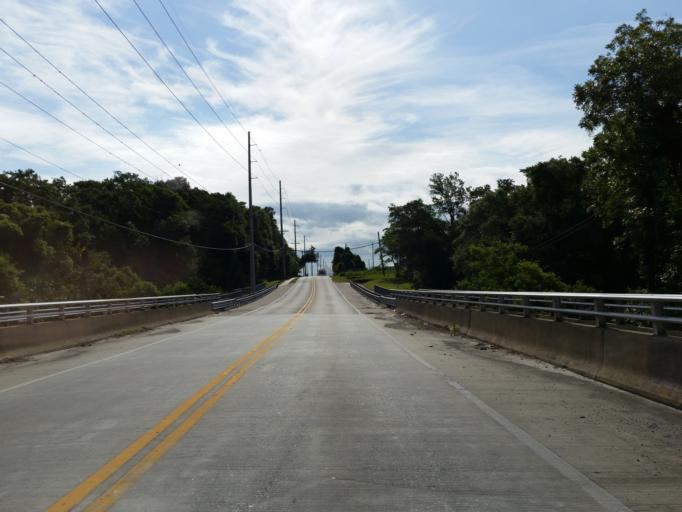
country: US
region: Florida
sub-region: Hillsborough County
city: Riverview
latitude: 27.8352
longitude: -82.3466
